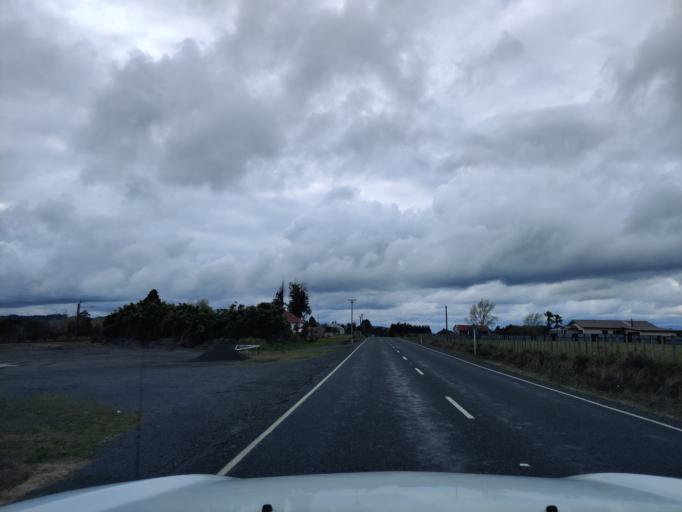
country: NZ
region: Waikato
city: Turangi
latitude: -39.0077
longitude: 175.3773
